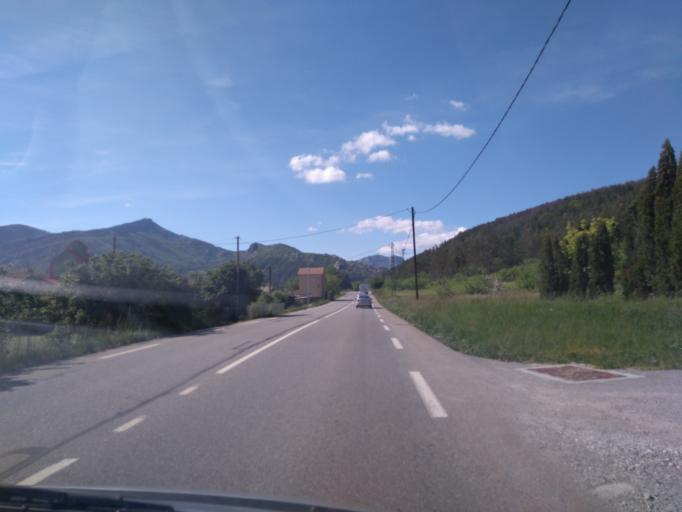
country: FR
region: Provence-Alpes-Cote d'Azur
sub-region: Departement des Hautes-Alpes
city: Serres
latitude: 44.4116
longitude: 5.7256
